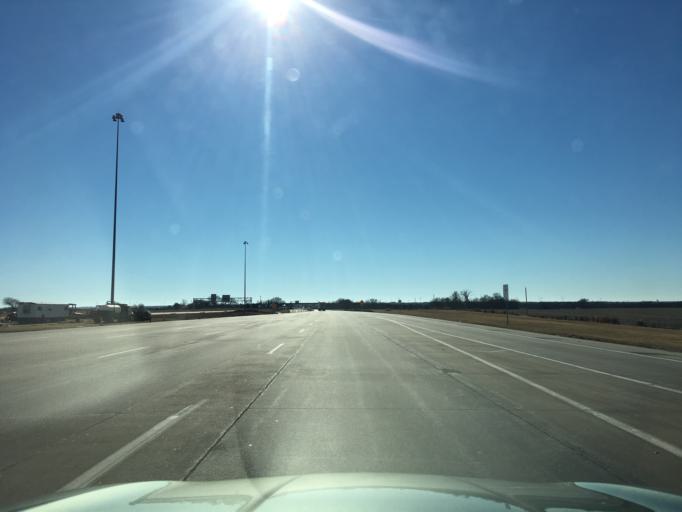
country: US
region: Kansas
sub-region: Sumner County
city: Wellington
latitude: 37.2388
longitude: -97.3393
